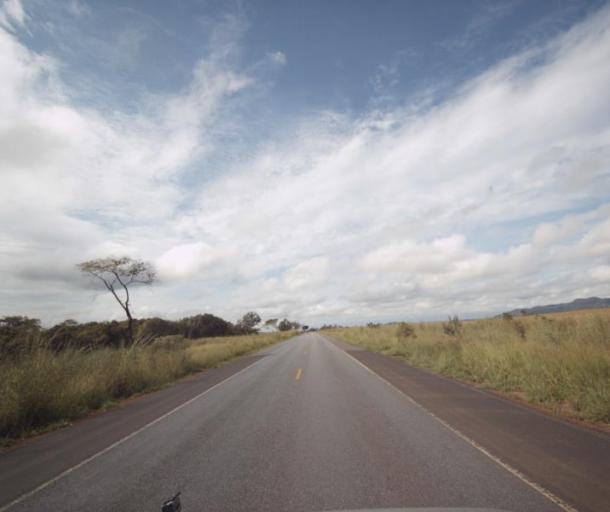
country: BR
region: Goias
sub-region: Padre Bernardo
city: Padre Bernardo
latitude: -15.4566
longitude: -48.6149
